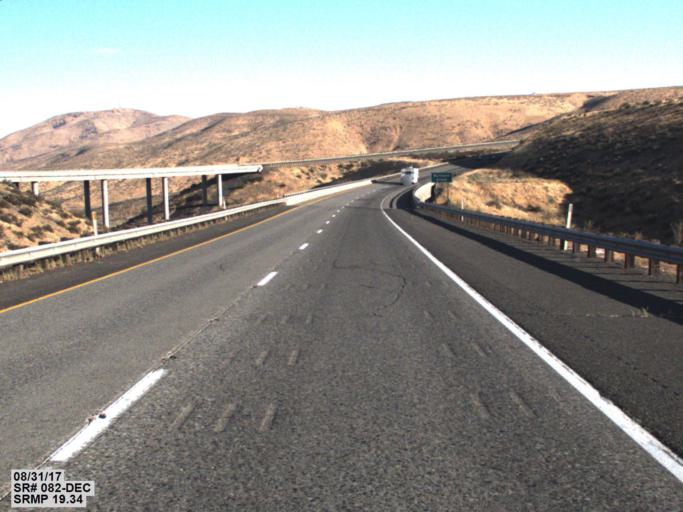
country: US
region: Washington
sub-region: Yakima County
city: Terrace Heights
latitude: 46.7451
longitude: -120.3884
